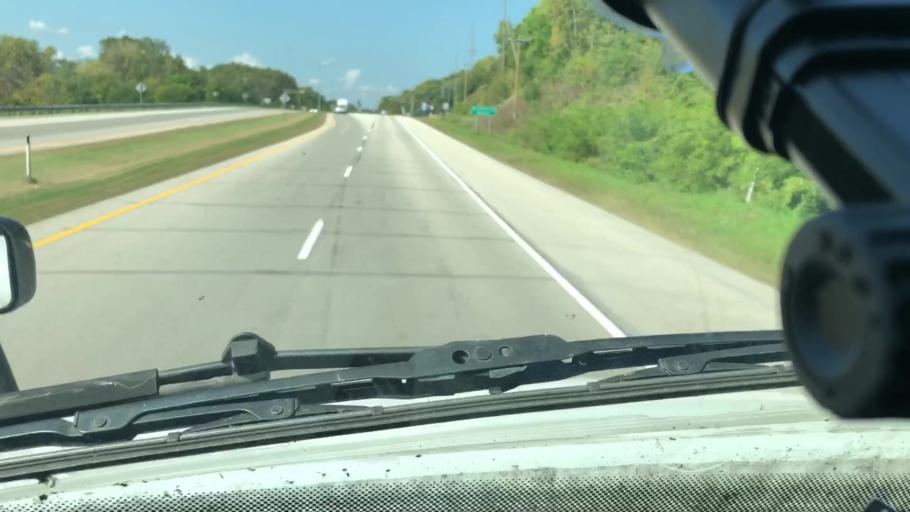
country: US
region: Minnesota
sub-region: Winona County
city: Winona
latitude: 44.0726
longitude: -91.6283
